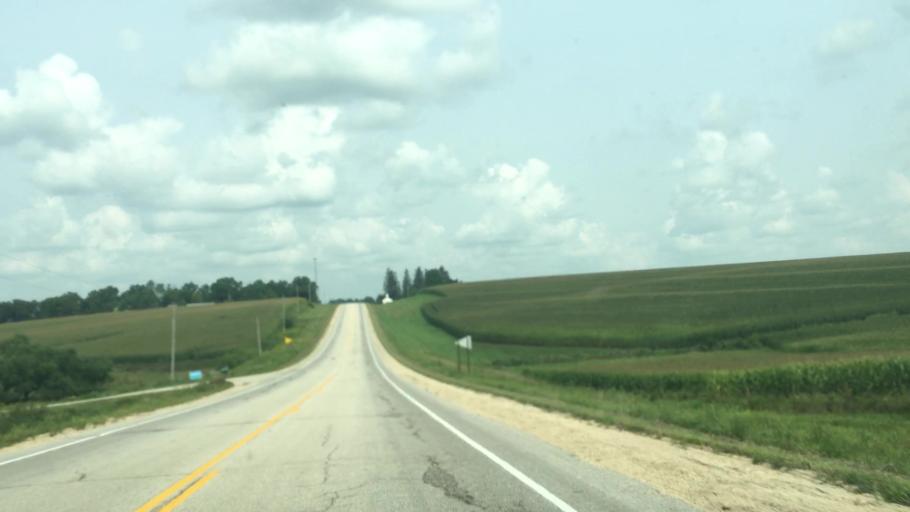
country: US
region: Minnesota
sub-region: Fillmore County
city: Harmony
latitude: 43.6544
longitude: -91.9301
